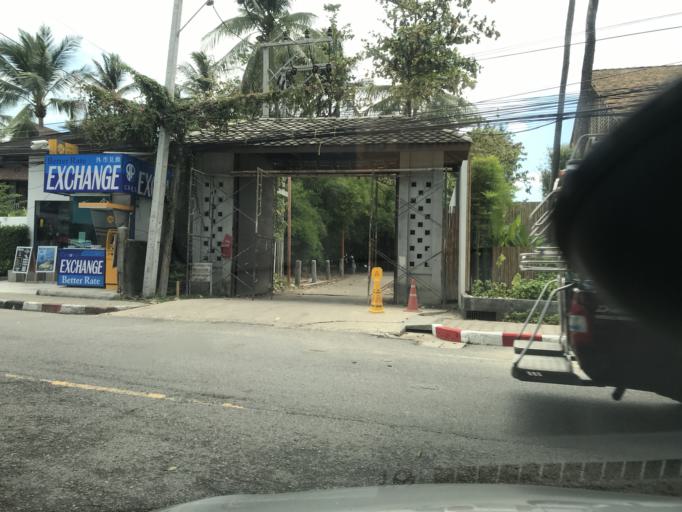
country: TH
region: Surat Thani
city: Ko Samui
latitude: 9.5372
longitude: 100.0695
